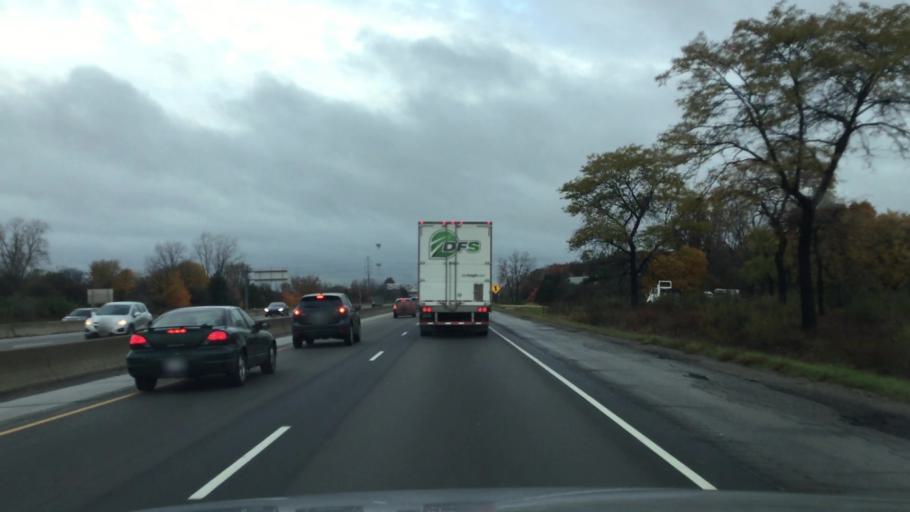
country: US
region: Michigan
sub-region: Washtenaw County
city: Ann Arbor
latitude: 42.2270
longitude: -83.6884
